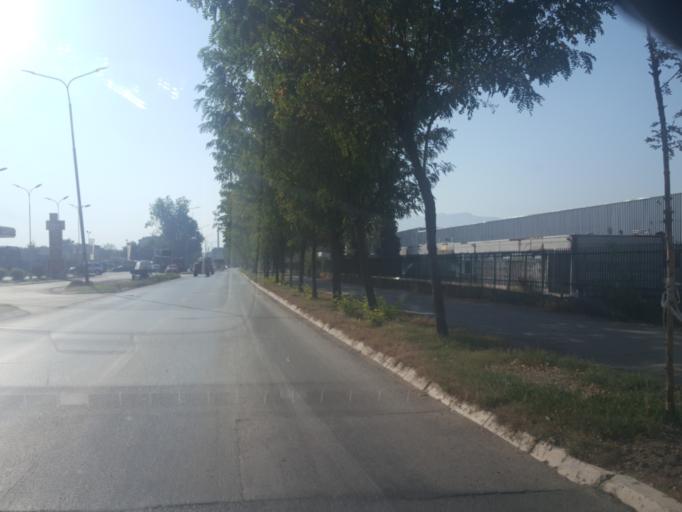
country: XK
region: Gjakova
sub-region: Komuna e Gjakoves
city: Gjakove
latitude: 42.3954
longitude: 20.4210
